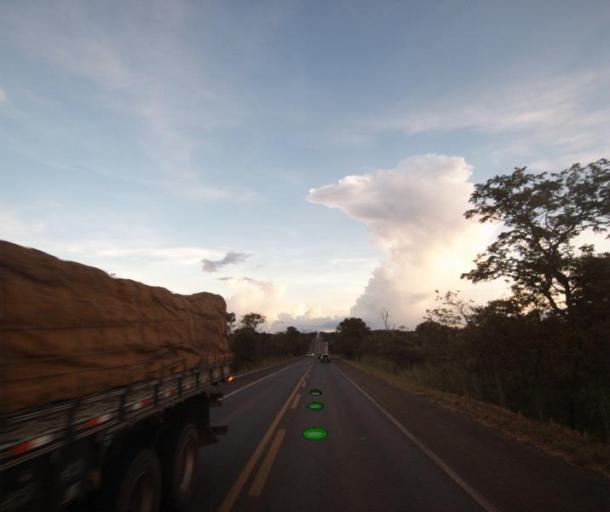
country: BR
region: Goias
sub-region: Uruacu
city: Uruacu
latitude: -14.4415
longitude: -49.1567
